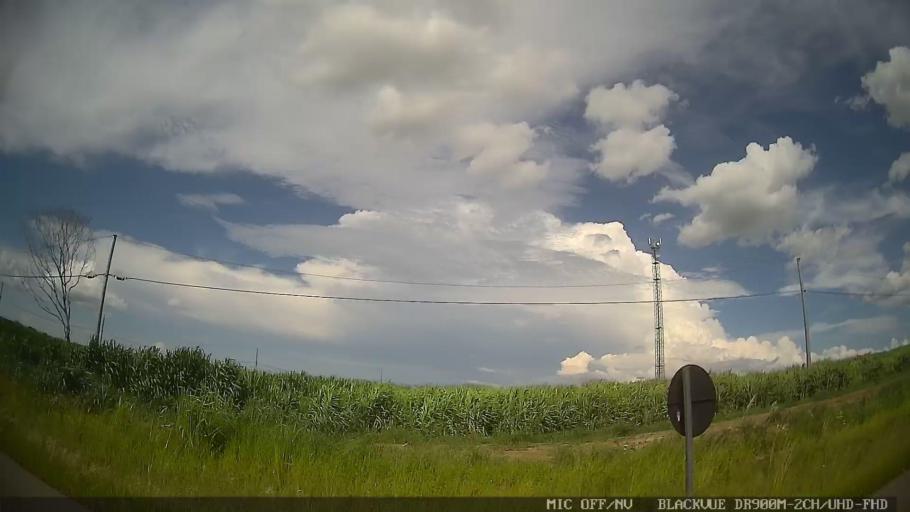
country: BR
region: Sao Paulo
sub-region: Conchas
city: Conchas
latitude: -23.0463
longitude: -47.9593
